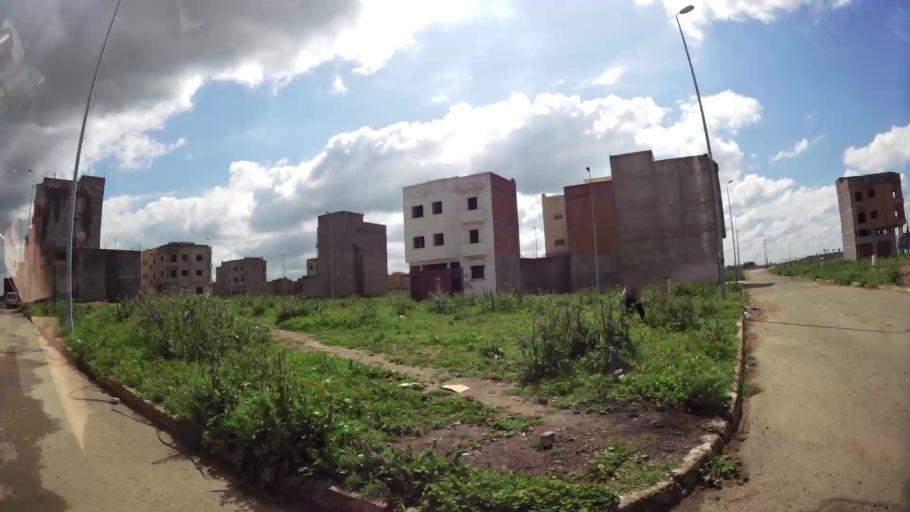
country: MA
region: Grand Casablanca
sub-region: Mediouna
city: Mediouna
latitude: 33.3669
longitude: -7.5298
